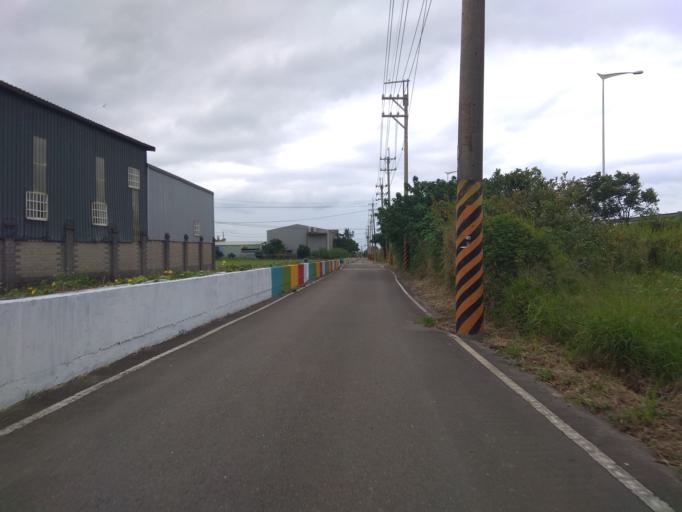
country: TW
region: Taiwan
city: Taoyuan City
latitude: 25.0425
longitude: 121.2203
